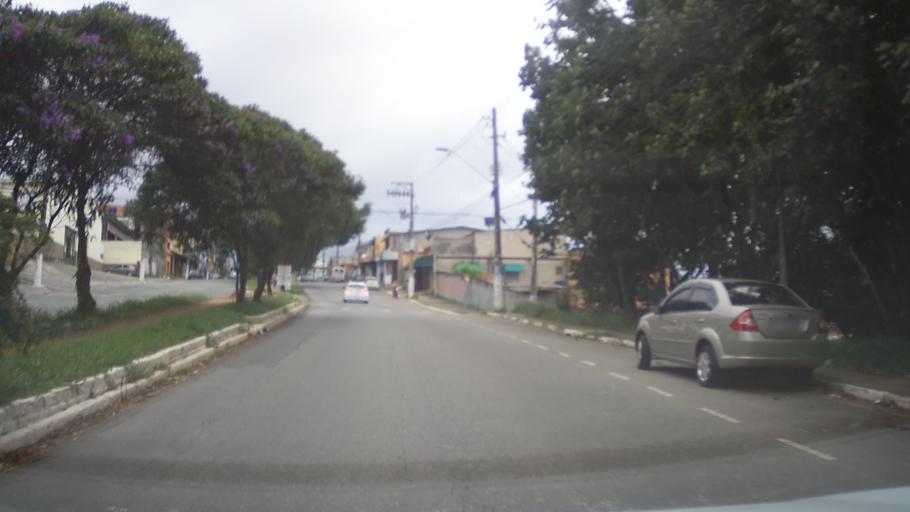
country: BR
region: Sao Paulo
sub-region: Aruja
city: Aruja
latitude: -23.4062
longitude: -46.4136
